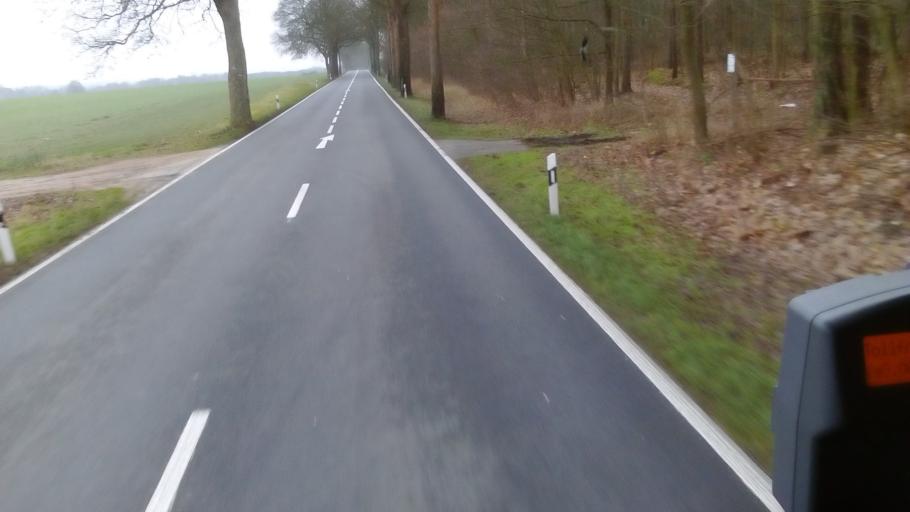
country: DE
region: Brandenburg
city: Heiligengrabe
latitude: 53.1391
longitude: 12.3193
